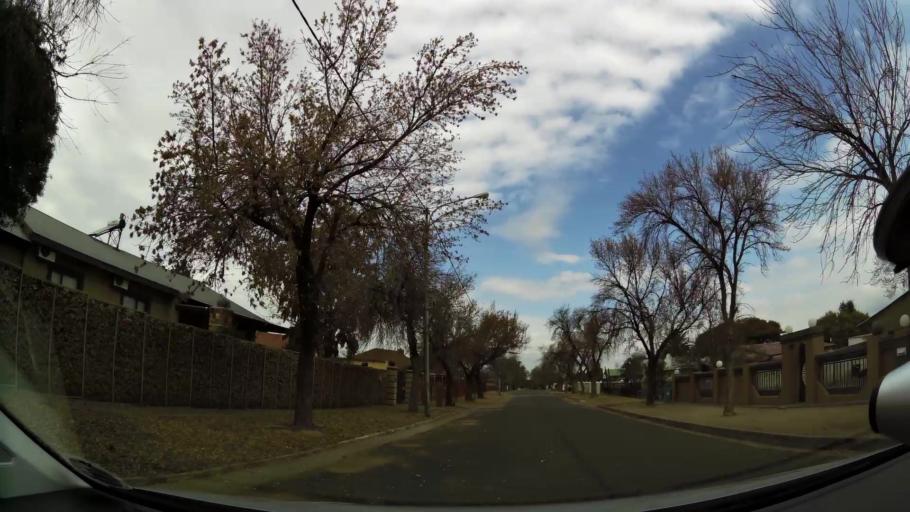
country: ZA
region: Orange Free State
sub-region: Fezile Dabi District Municipality
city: Kroonstad
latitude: -27.6371
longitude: 27.2299
